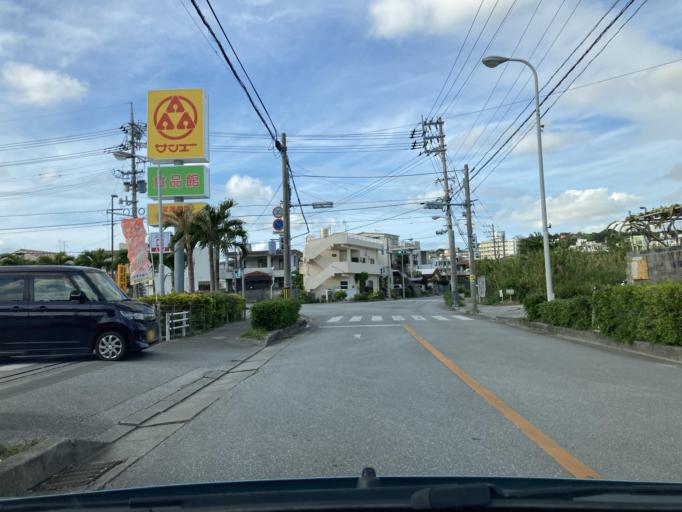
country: JP
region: Okinawa
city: Itoman
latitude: 26.1261
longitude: 127.6773
